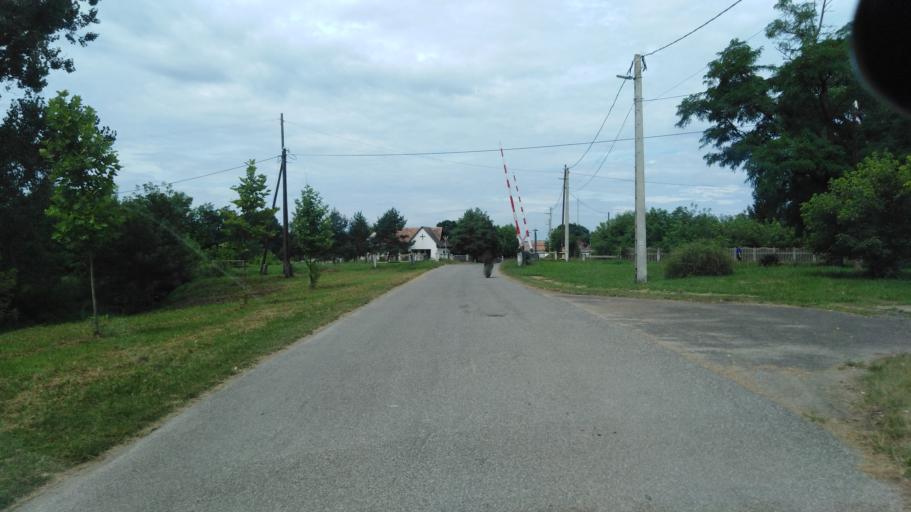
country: HU
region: Nograd
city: Karancskeszi
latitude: 48.2356
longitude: 19.6293
